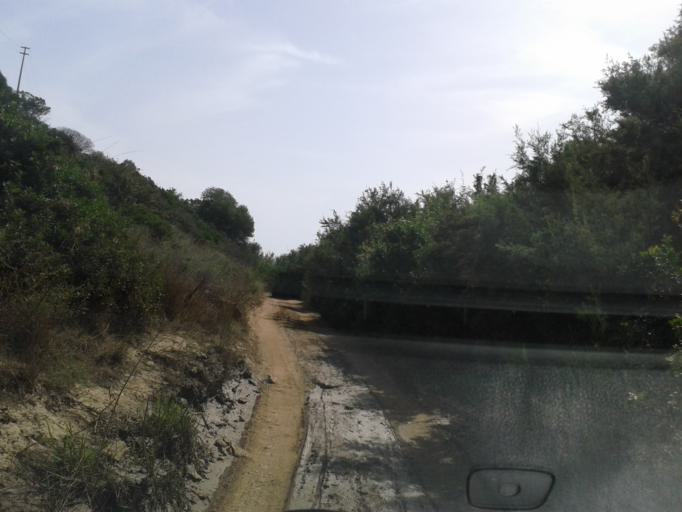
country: IT
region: Sardinia
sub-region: Provincia di Cagliari
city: Villasimius
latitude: 39.1366
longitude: 9.4889
